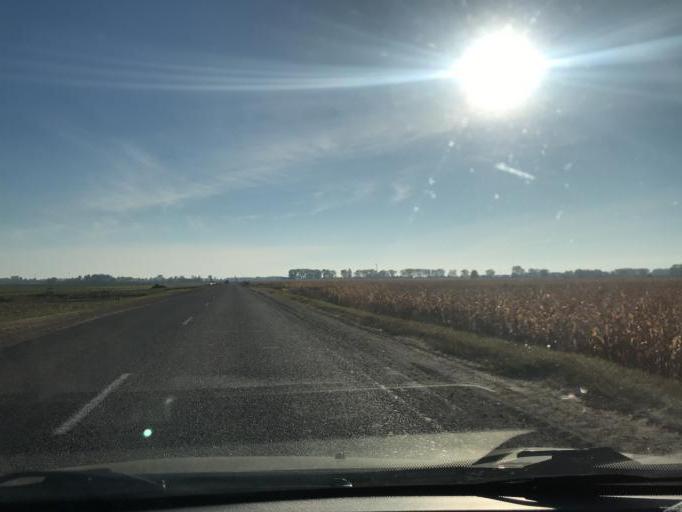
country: BY
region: Gomel
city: Brahin
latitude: 51.7802
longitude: 30.2307
